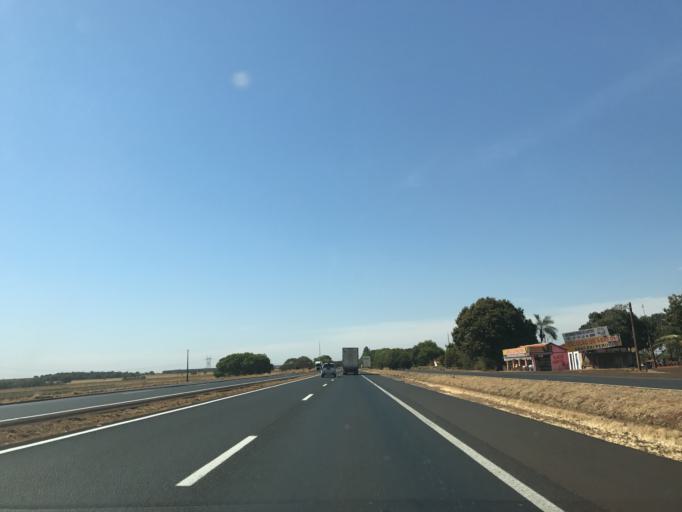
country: BR
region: Minas Gerais
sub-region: Centralina
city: Centralina
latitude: -18.7161
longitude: -49.1302
